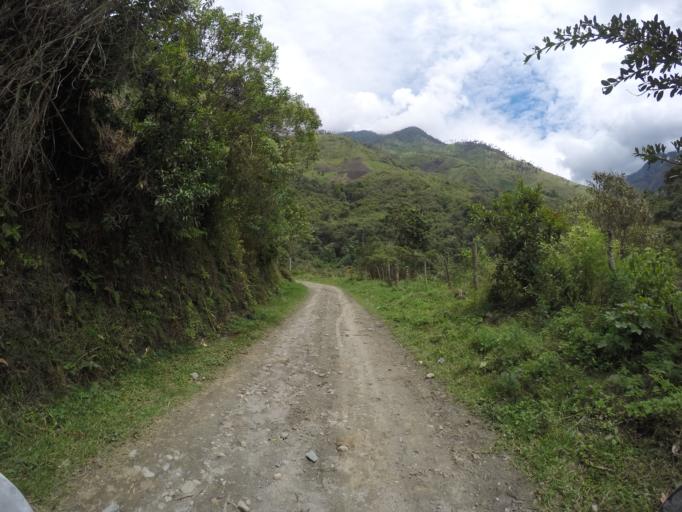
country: CO
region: Tolima
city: Cajamarca
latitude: 4.5217
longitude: -75.4095
